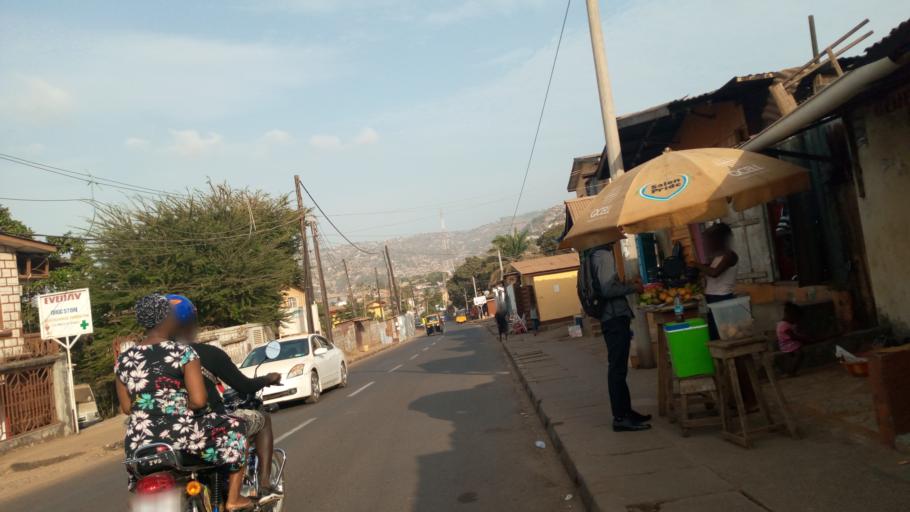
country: SL
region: Western Area
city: Freetown
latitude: 8.4747
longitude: -13.2543
